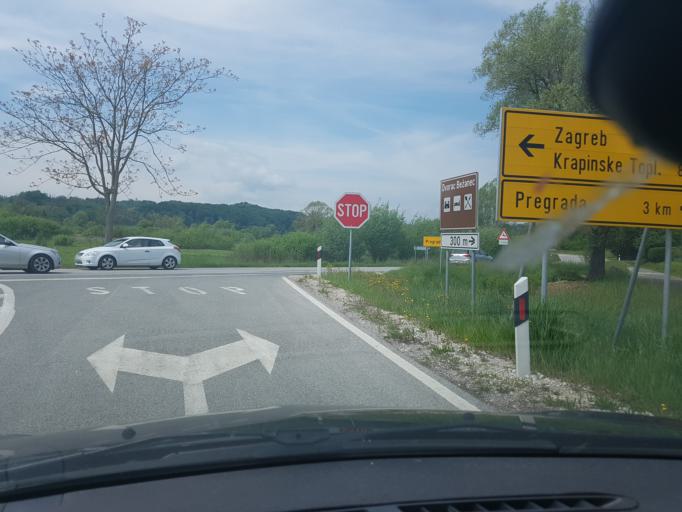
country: HR
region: Krapinsko-Zagorska
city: Pregrada
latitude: 46.1446
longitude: 15.7813
